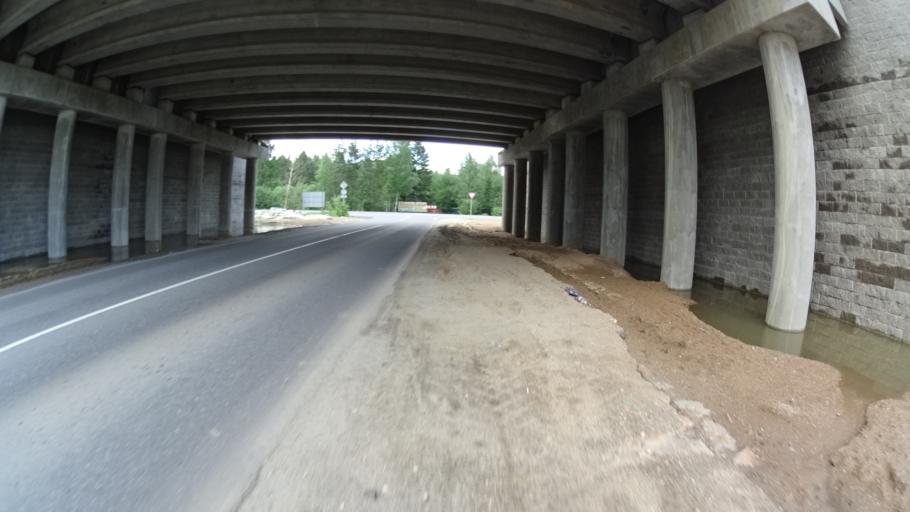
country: RU
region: Moskovskaya
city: Zelenogradskiy
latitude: 56.1266
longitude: 37.9008
